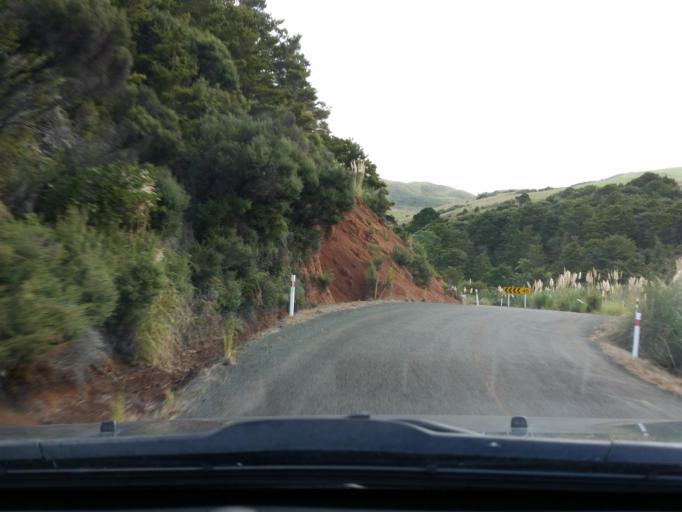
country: NZ
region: Northland
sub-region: Kaipara District
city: Dargaville
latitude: -35.7664
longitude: 173.6069
